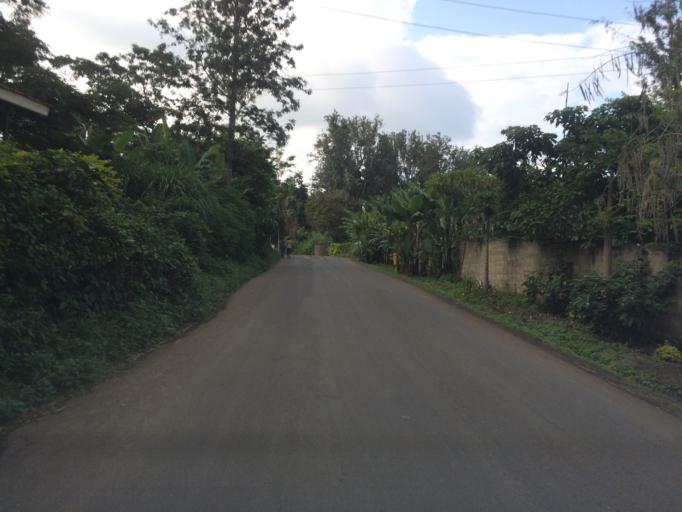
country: TZ
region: Arusha
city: Usa River
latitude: -3.3637
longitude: 36.8160
